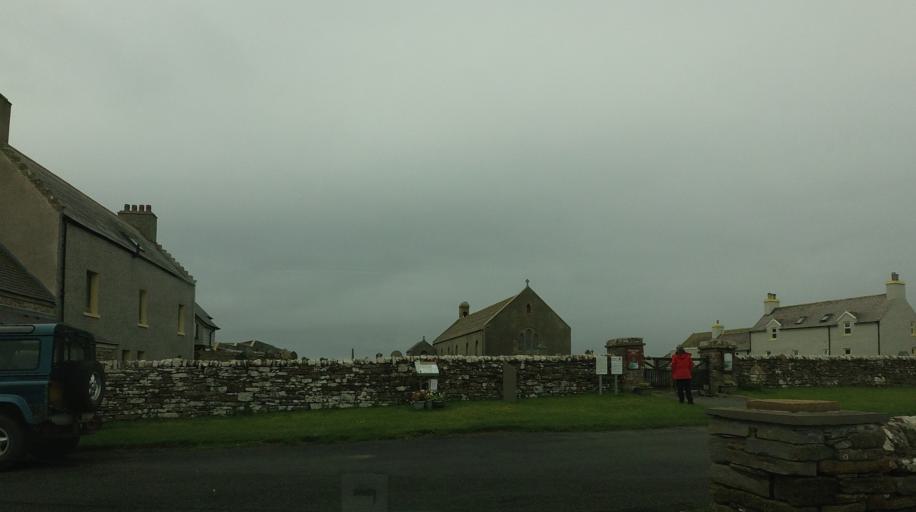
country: GB
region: Scotland
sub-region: Orkney Islands
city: Stromness
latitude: 59.1293
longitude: -3.3154
